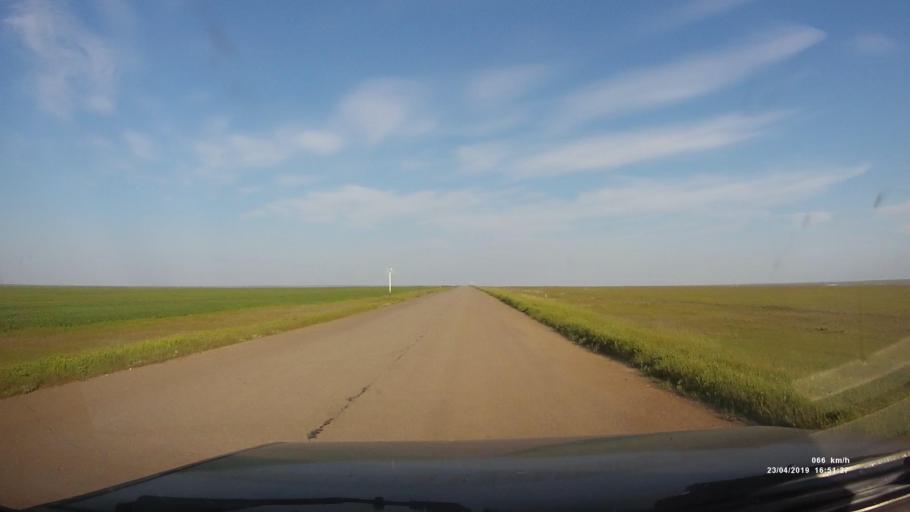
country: RU
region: Kalmykiya
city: Priyutnoye
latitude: 46.3231
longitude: 43.3061
